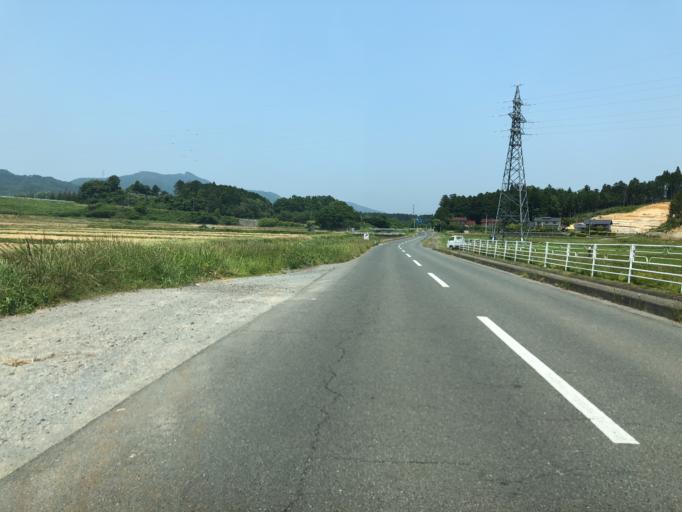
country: JP
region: Miyagi
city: Marumori
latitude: 37.8329
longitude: 140.8954
